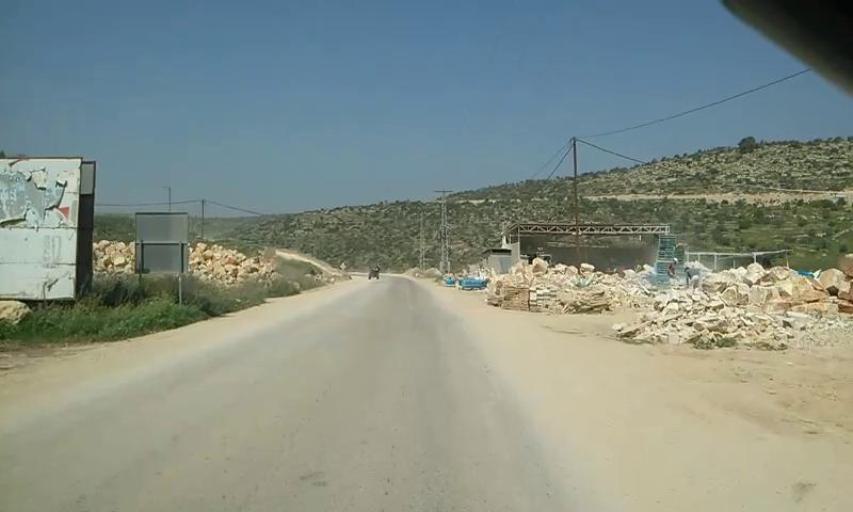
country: PS
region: West Bank
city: Az Zababidah
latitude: 32.4027
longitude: 35.3172
